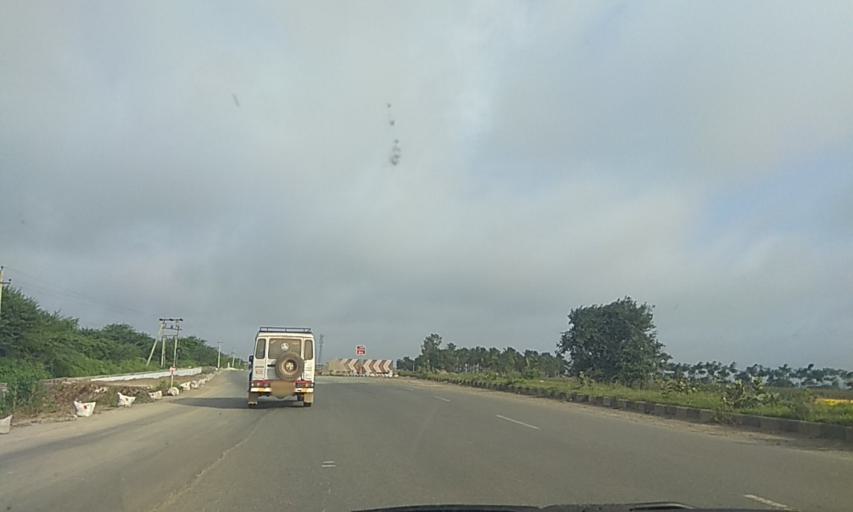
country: IN
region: Karnataka
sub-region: Haveri
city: Haveri
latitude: 14.7699
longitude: 75.4247
